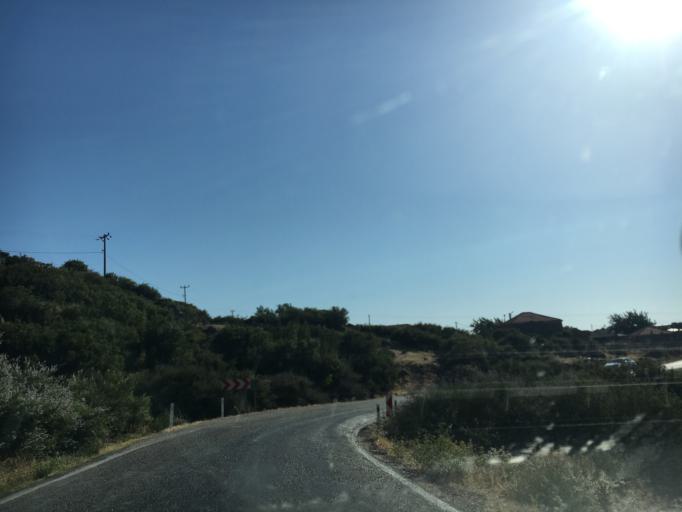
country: TR
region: Canakkale
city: Behram
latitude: 39.4941
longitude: 26.3337
